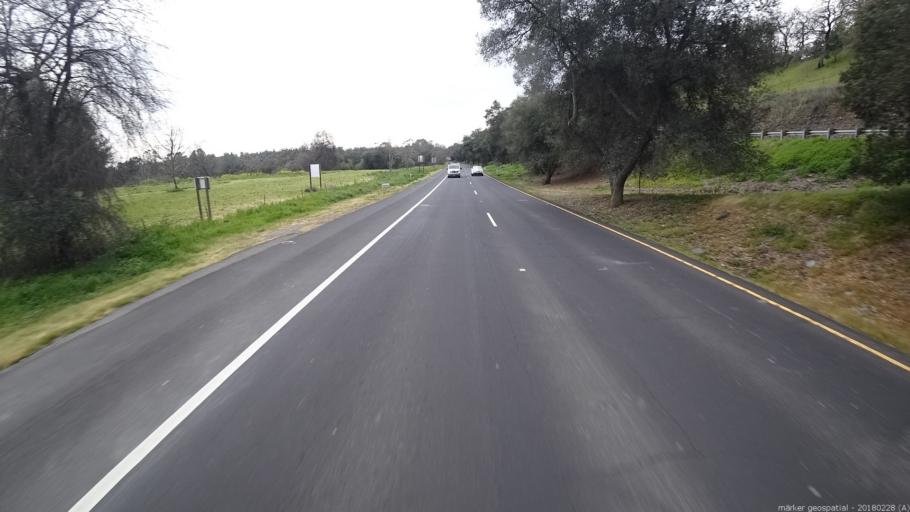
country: US
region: California
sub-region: Sacramento County
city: Folsom
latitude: 38.6824
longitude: -121.1860
